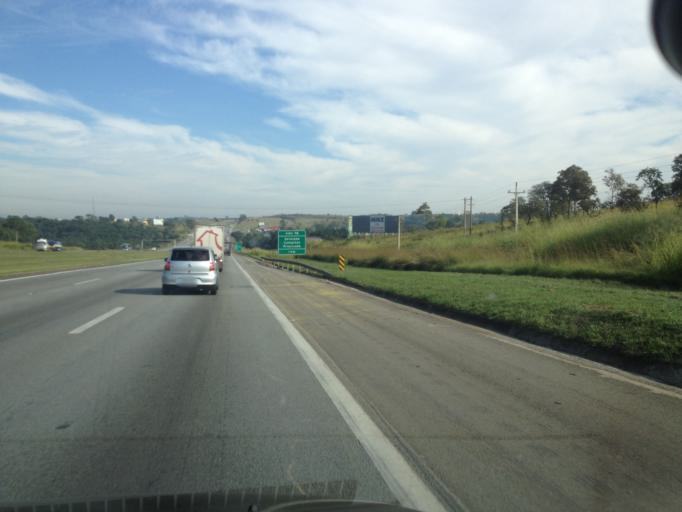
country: BR
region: Sao Paulo
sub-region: Itu
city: Itu
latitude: -23.4036
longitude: -47.3172
